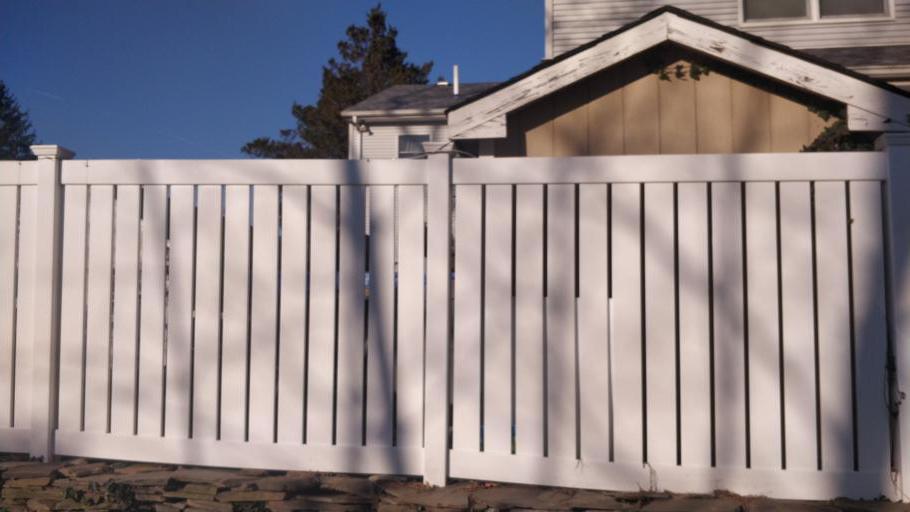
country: US
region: New York
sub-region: Nassau County
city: Bayville
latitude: 40.9046
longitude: -73.5724
